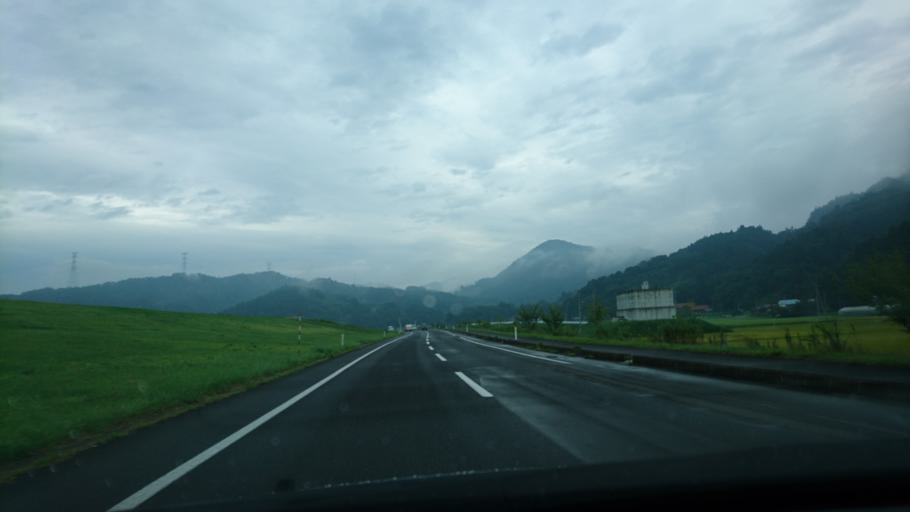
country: JP
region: Iwate
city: Ichinoseki
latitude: 38.9245
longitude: 141.2567
